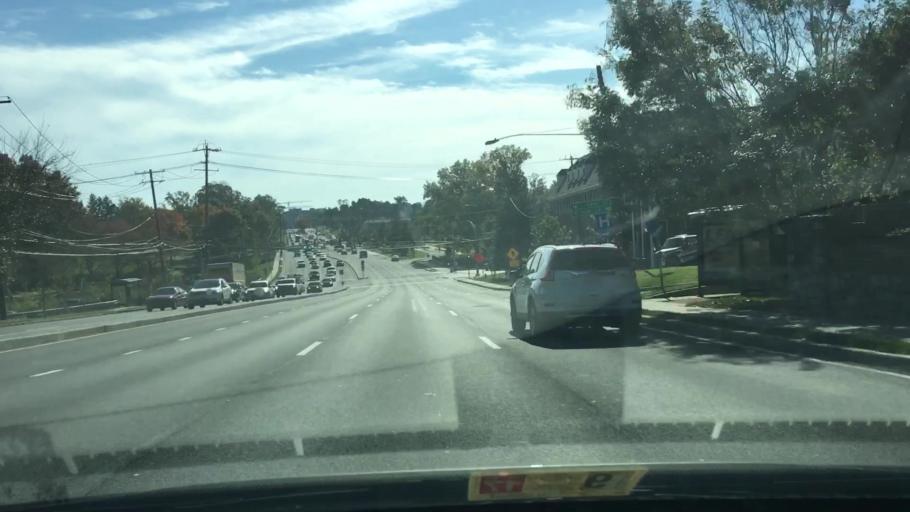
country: US
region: Maryland
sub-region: Montgomery County
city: South Kensington
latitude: 39.0078
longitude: -77.0976
